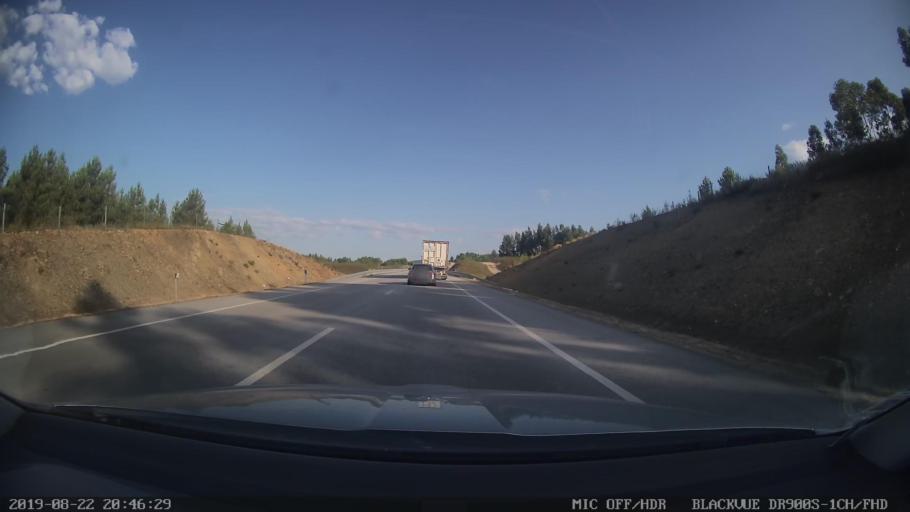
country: PT
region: Castelo Branco
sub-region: Proenca-A-Nova
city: Proenca-a-Nova
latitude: 39.7270
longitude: -7.8770
